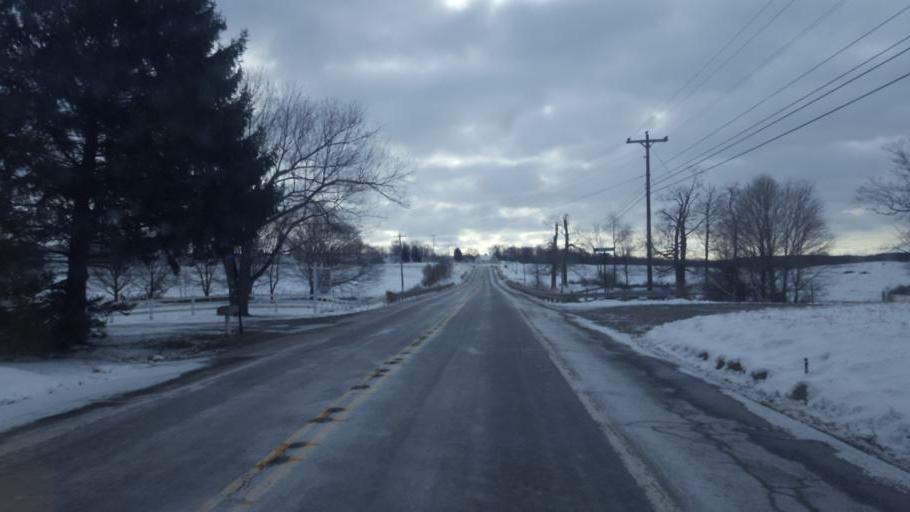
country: US
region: Pennsylvania
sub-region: Lawrence County
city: New Wilmington
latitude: 41.1182
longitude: -80.2827
